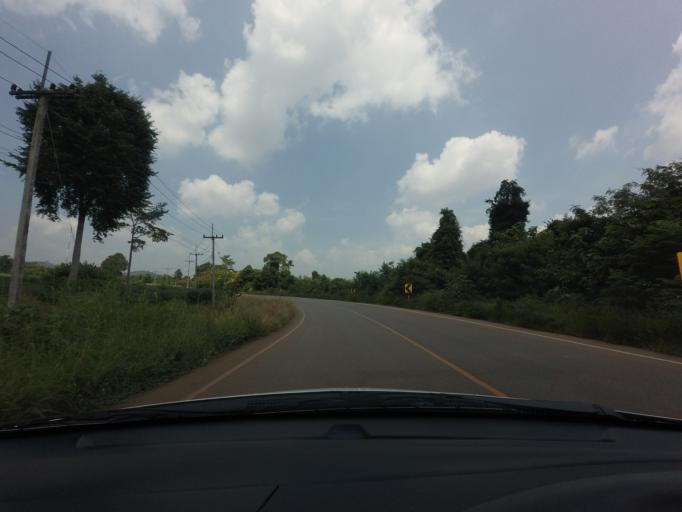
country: TH
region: Nakhon Ratchasima
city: Pak Chong
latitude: 14.5802
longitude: 101.5667
